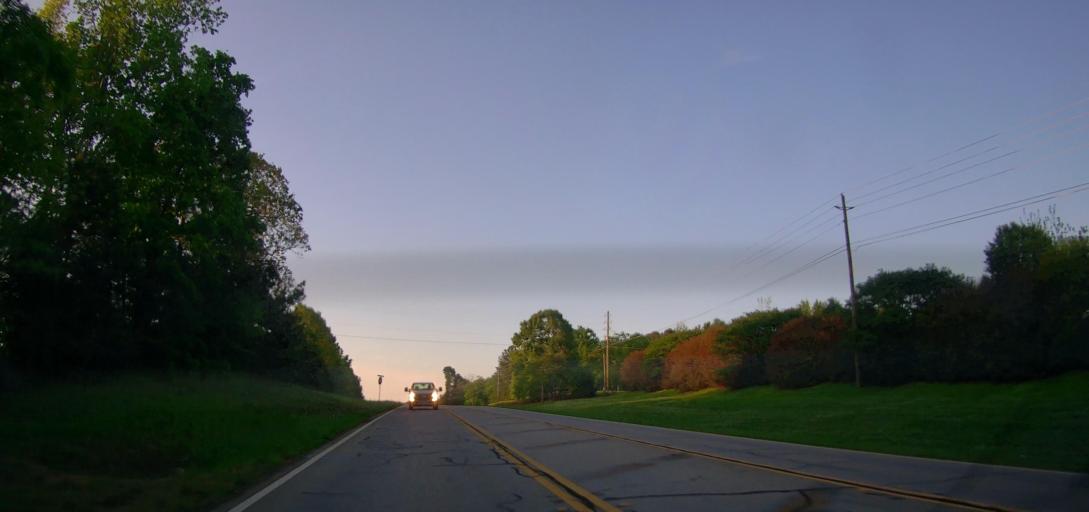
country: US
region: Georgia
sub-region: Newton County
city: Oakwood
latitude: 33.5079
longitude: -83.9481
